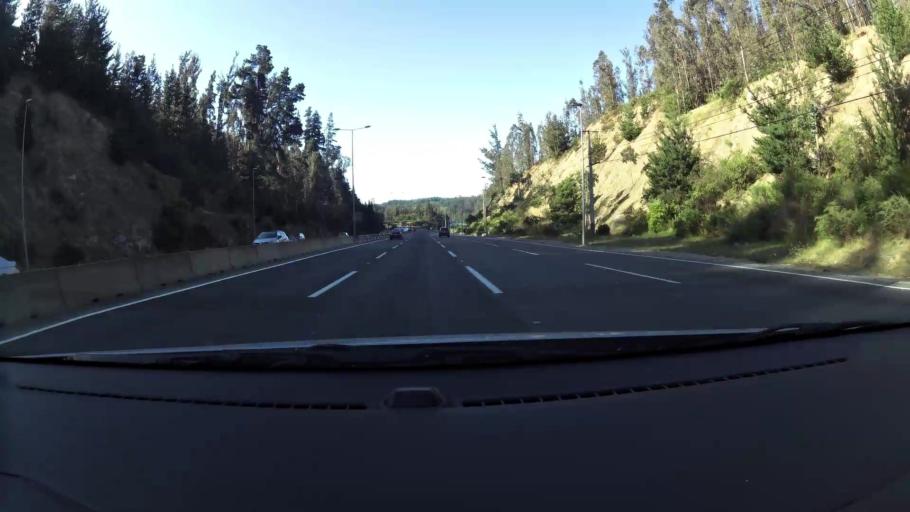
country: CL
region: Valparaiso
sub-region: Provincia de Valparaiso
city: Vina del Mar
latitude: -33.1033
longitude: -71.5481
